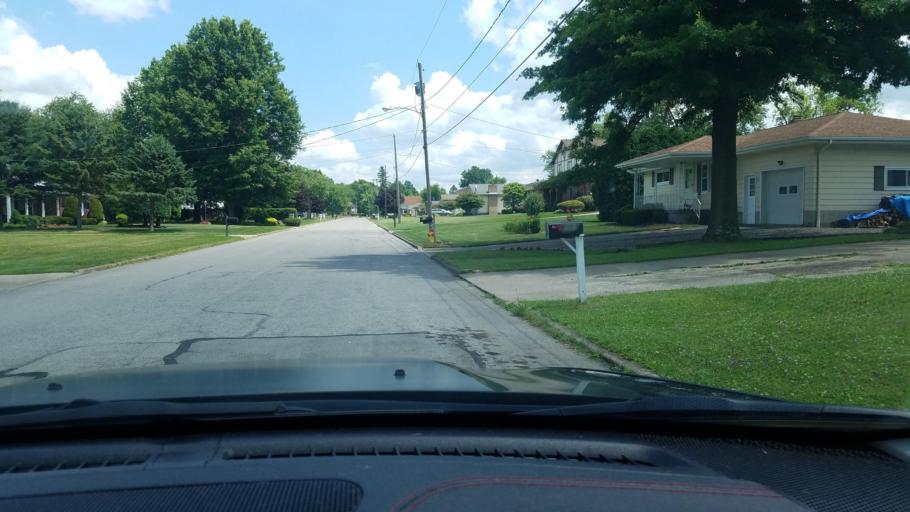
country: US
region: Ohio
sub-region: Mahoning County
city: Campbell
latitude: 41.0776
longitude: -80.5817
